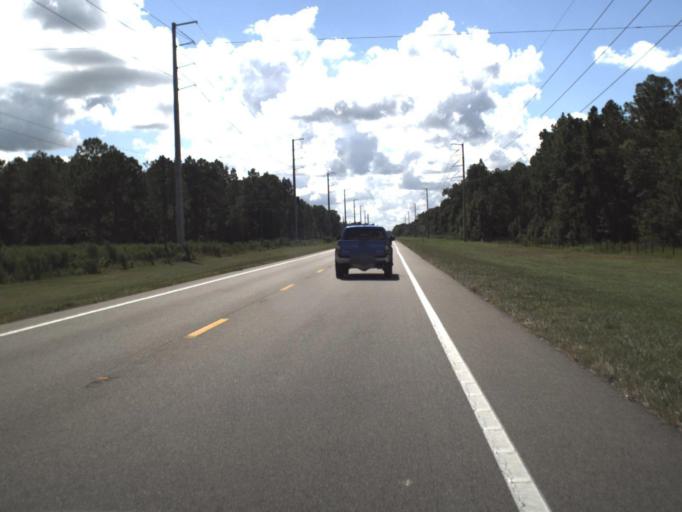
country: US
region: Florida
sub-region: Polk County
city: Kathleen
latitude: 28.2365
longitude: -82.0417
